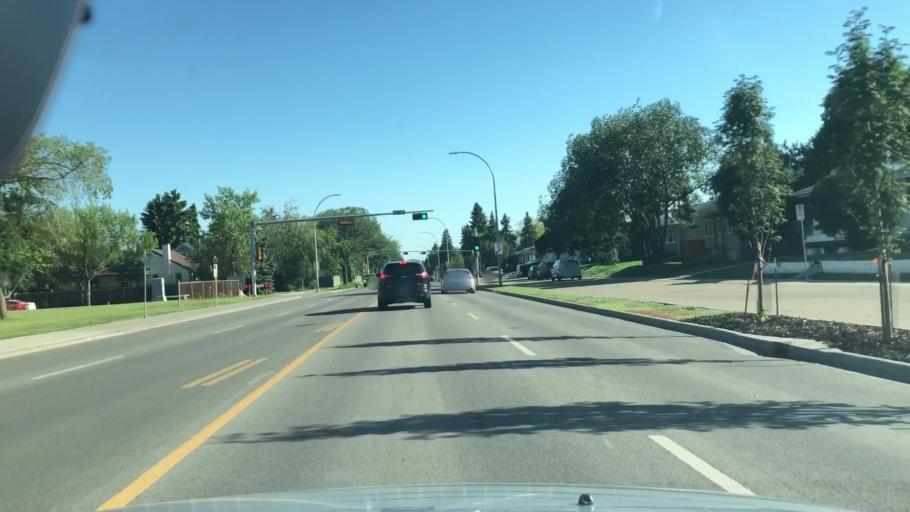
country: CA
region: Alberta
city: Edmonton
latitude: 53.5785
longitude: -113.5413
